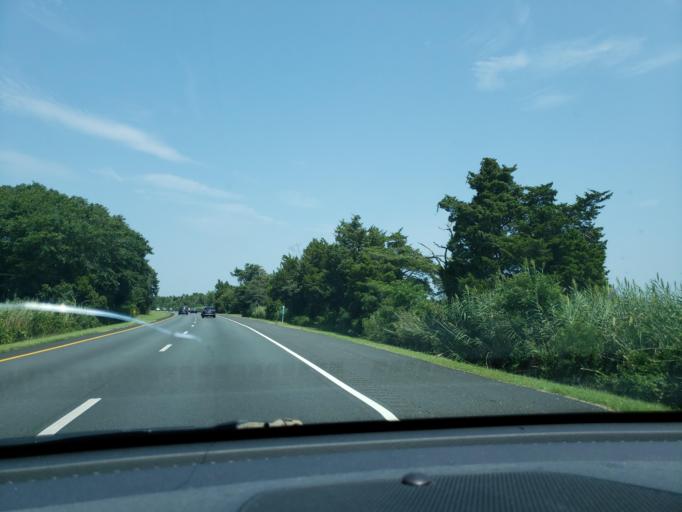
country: US
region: New Jersey
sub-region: Cape May County
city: Ocean City
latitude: 39.2746
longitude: -74.6295
